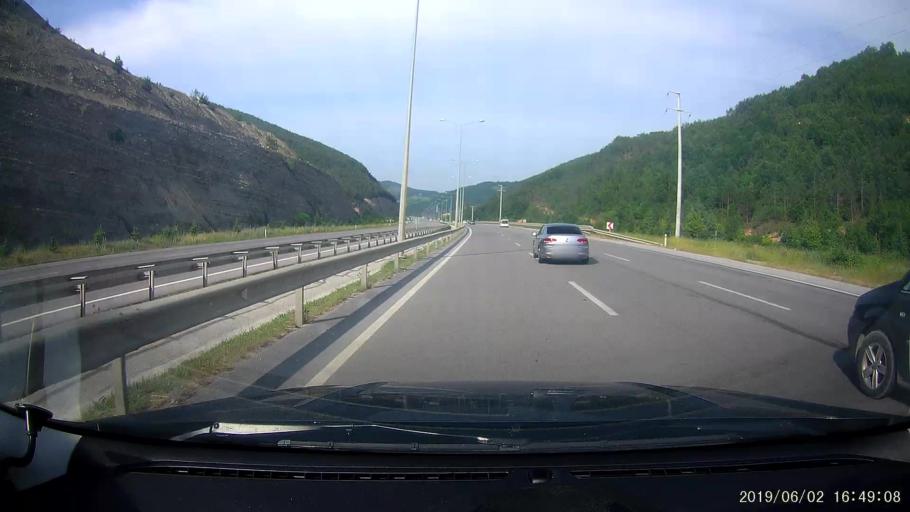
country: TR
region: Samsun
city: Taflan
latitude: 41.2335
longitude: 36.1549
